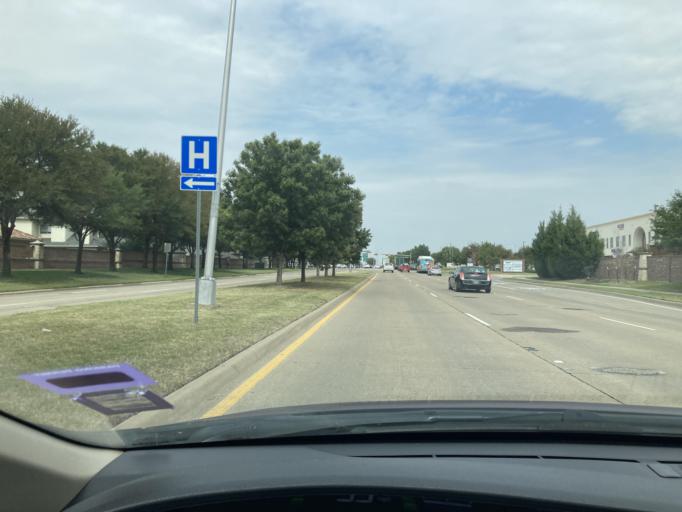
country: US
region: Texas
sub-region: Dallas County
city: Addison
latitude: 33.0401
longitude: -96.7945
